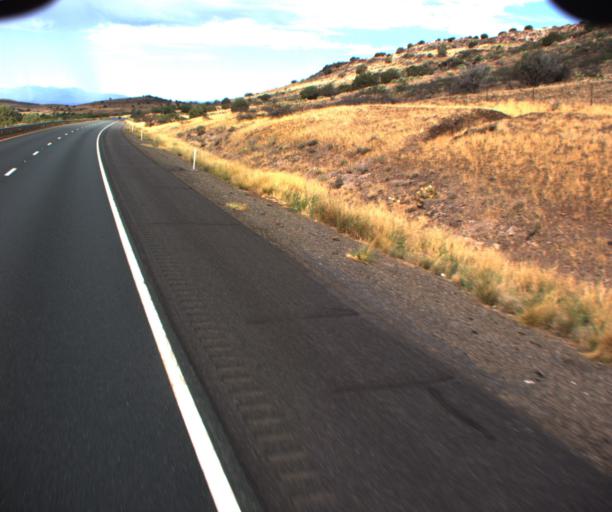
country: US
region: Arizona
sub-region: Yavapai County
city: Camp Verde
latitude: 34.4875
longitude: -112.0117
